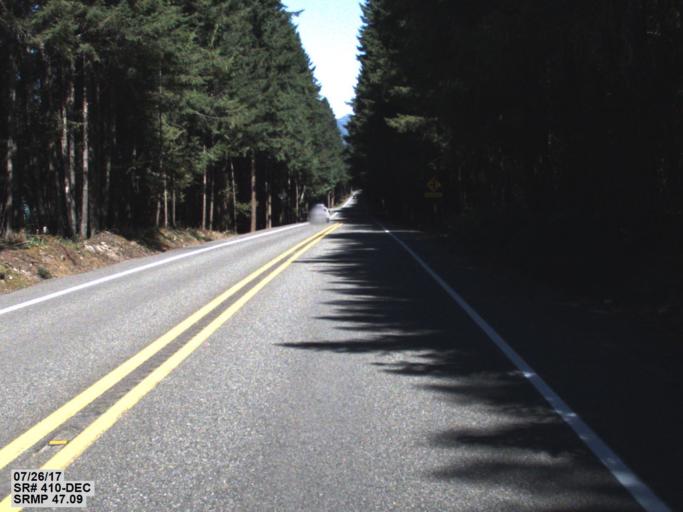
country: US
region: Washington
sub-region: King County
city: Riverbend
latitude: 47.1111
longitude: -121.6004
